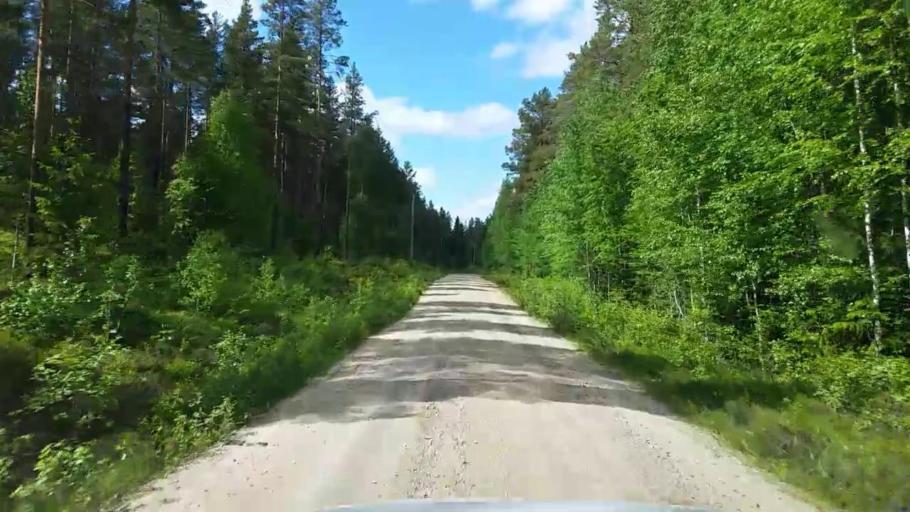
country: SE
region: Gaevleborg
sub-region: Ovanakers Kommun
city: Alfta
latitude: 61.5471
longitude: 15.9688
